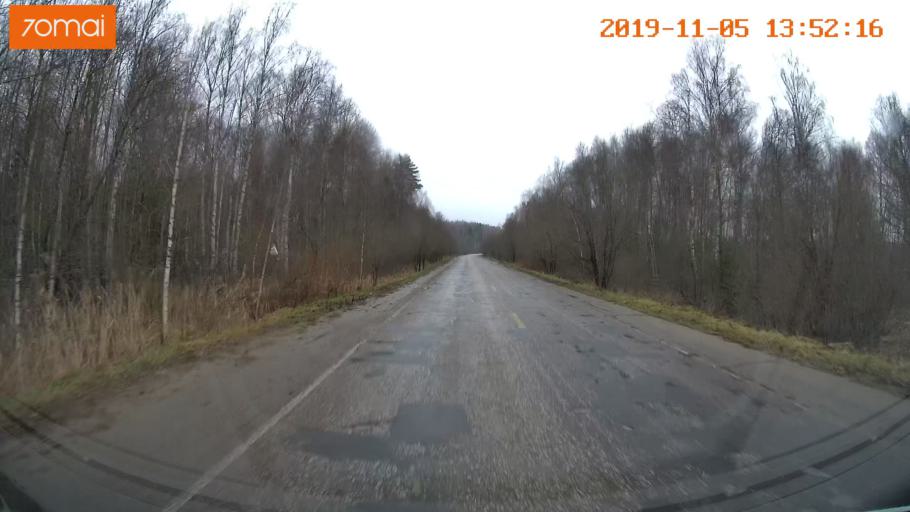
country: RU
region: Ivanovo
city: Kaminskiy
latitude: 57.0271
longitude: 41.3887
